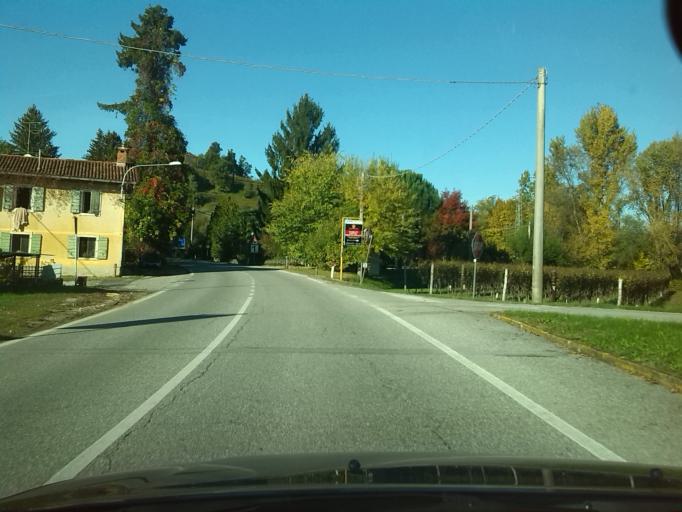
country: IT
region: Friuli Venezia Giulia
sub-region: Provincia di Udine
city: Corno di Rosazzo
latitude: 46.0012
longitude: 13.4695
